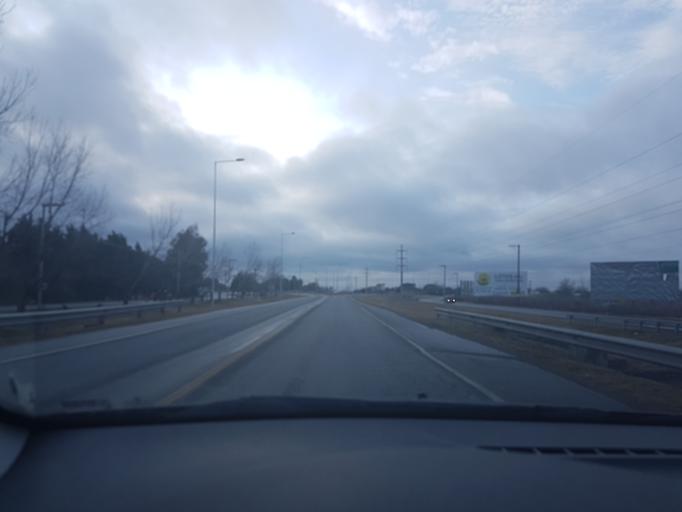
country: AR
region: Cordoba
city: Villa Allende
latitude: -31.3012
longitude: -64.2672
